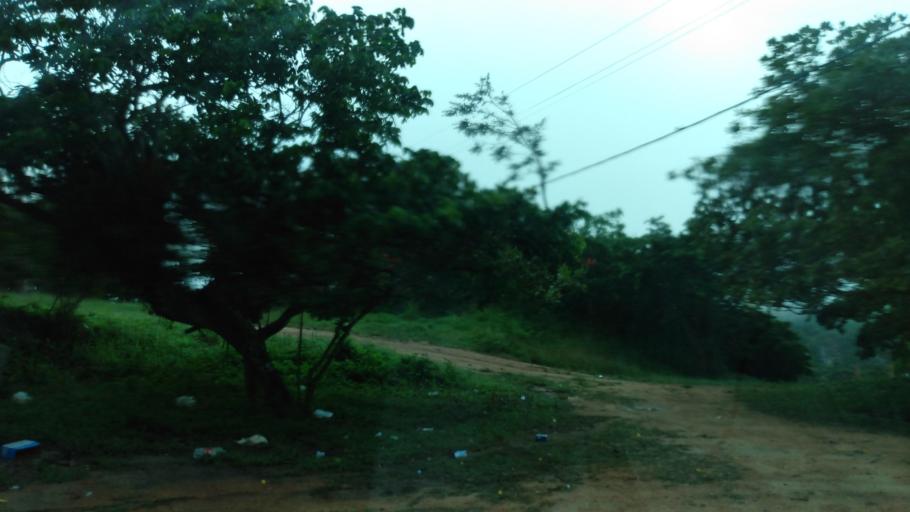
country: BR
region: Pernambuco
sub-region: Bezerros
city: Bezerros
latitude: -8.1639
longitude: -35.7694
